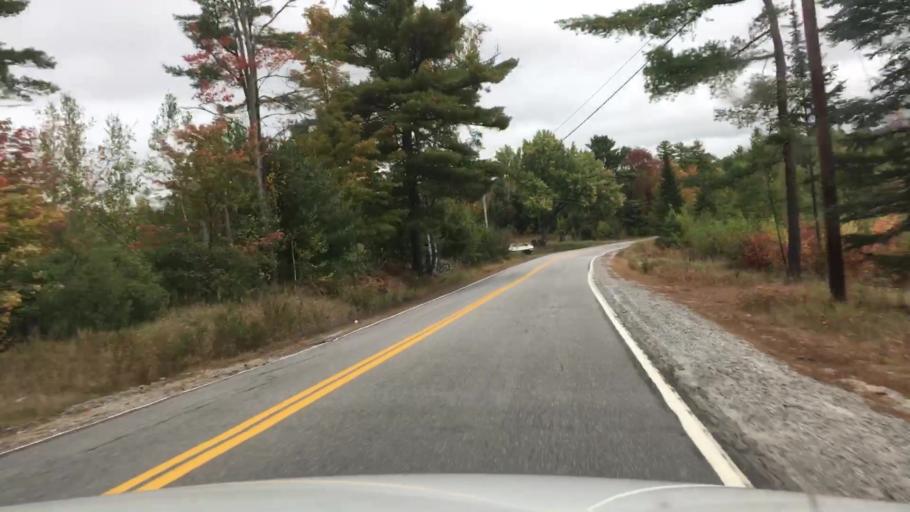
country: US
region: Maine
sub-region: Oxford County
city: Bethel
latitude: 44.3944
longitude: -70.7956
